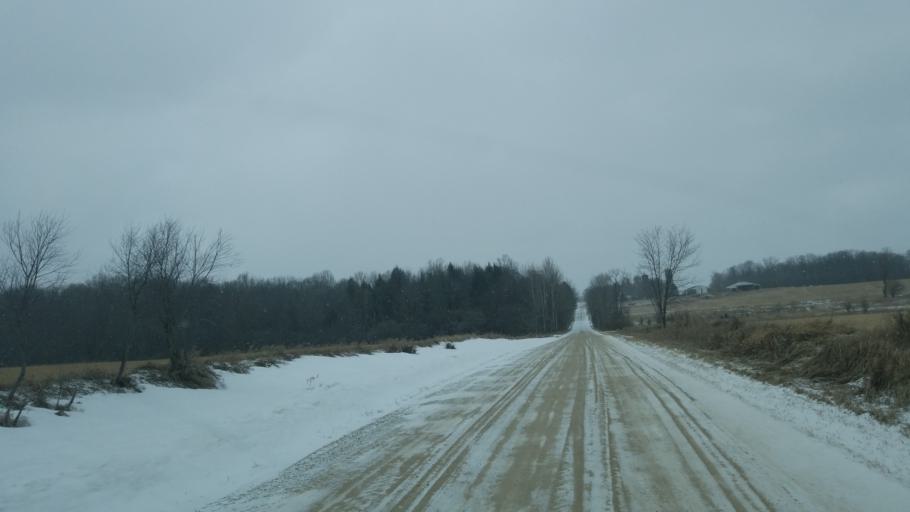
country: US
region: Michigan
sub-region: Osceola County
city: Evart
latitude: 44.0180
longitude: -85.2066
